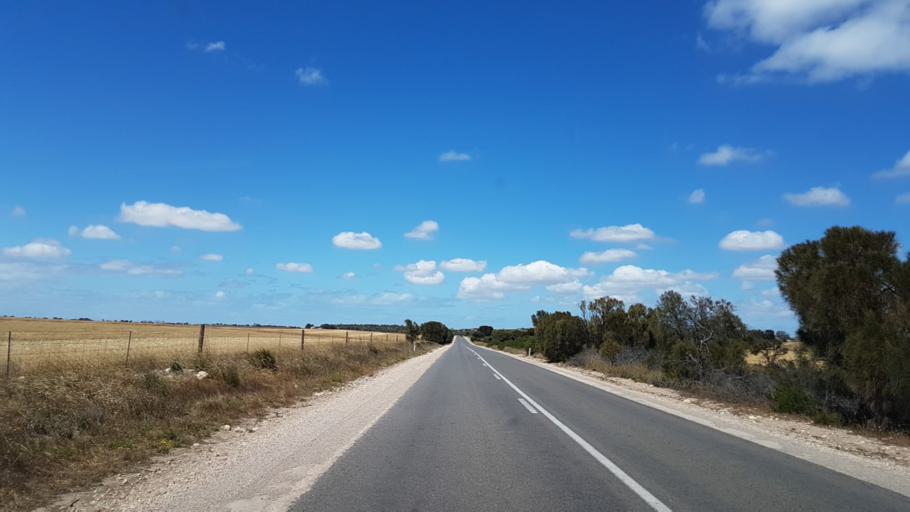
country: AU
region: South Australia
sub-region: Yorke Peninsula
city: Honiton
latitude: -34.9001
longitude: 137.4574
